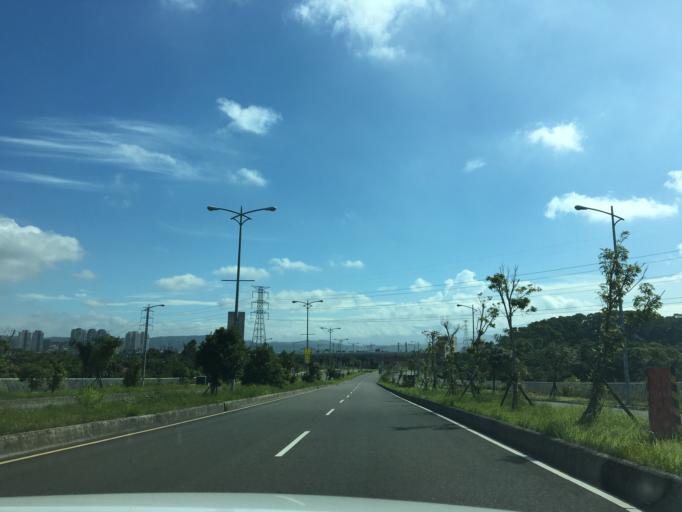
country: TW
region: Taiwan
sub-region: Hsinchu
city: Zhubei
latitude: 24.7949
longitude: 121.0168
